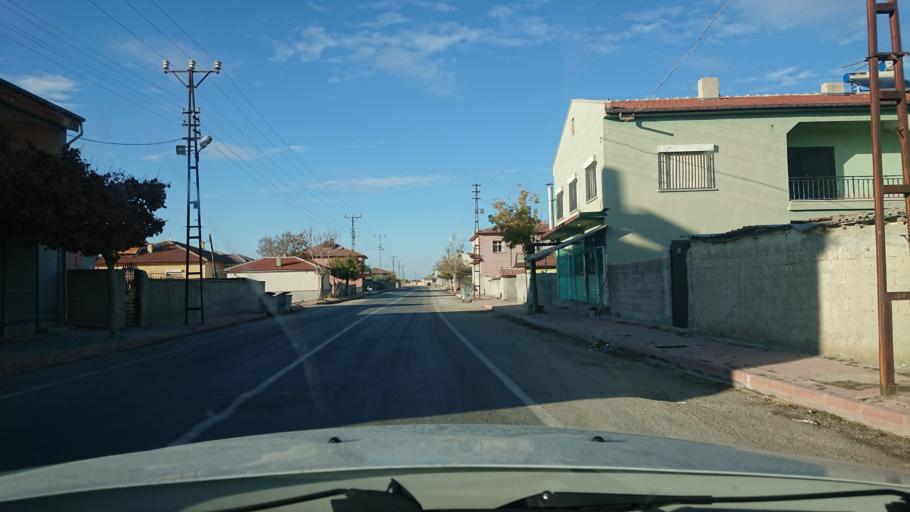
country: TR
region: Aksaray
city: Eskil
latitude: 38.5622
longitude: 33.1950
